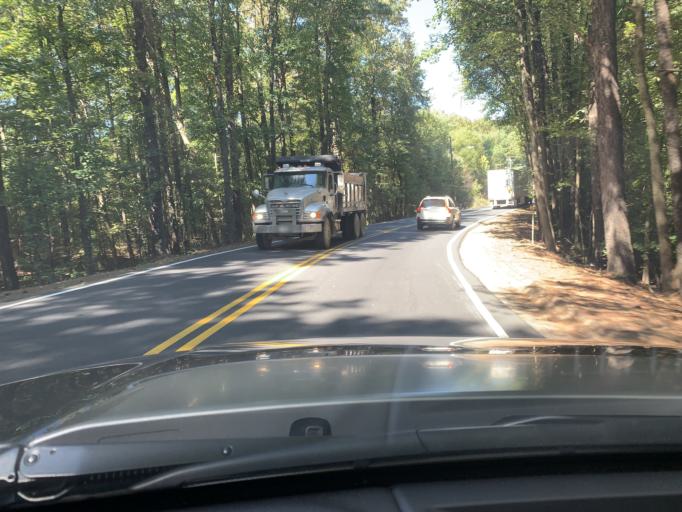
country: US
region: Georgia
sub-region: Clayton County
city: Conley
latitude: 33.6670
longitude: -84.3314
